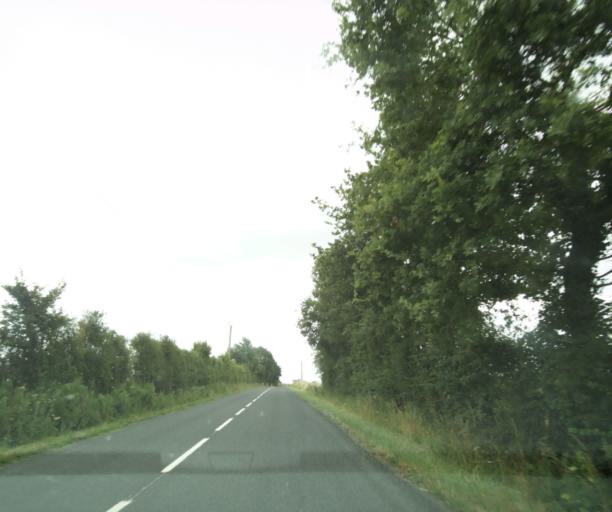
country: FR
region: Pays de la Loire
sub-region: Departement de Maine-et-Loire
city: Durtal
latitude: 47.7304
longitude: -0.2638
